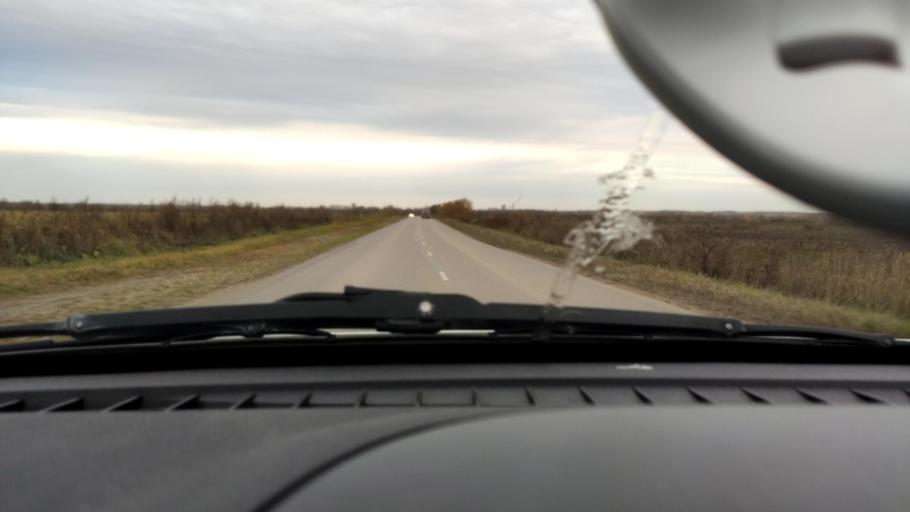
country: RU
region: Perm
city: Kondratovo
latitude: 57.9922
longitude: 56.0917
